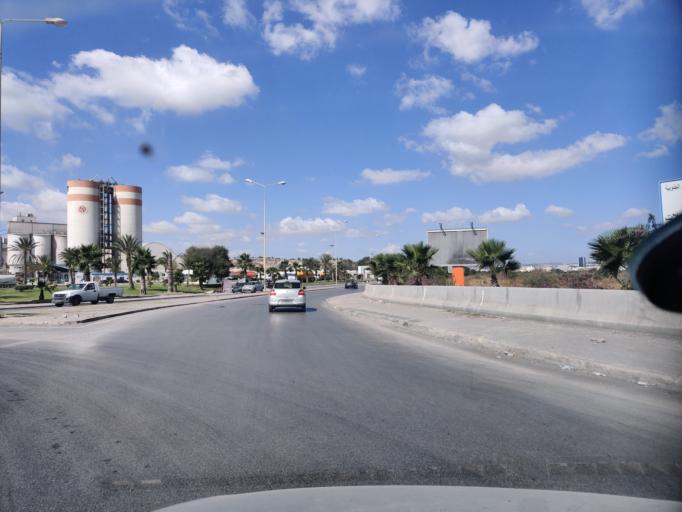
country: TN
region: Bin 'Arus
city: Ben Arous
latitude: 36.7782
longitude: 10.2065
